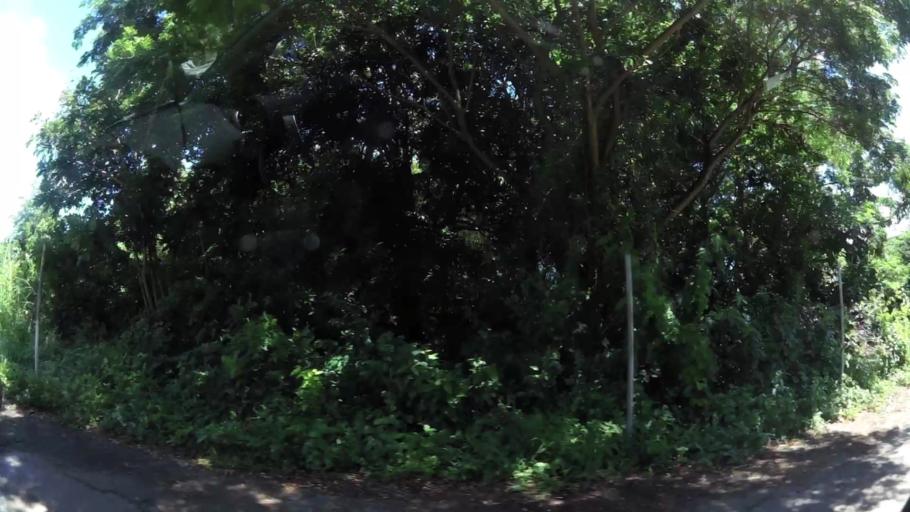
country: TT
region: Tobago
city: Scarborough
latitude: 11.1789
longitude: -60.7813
